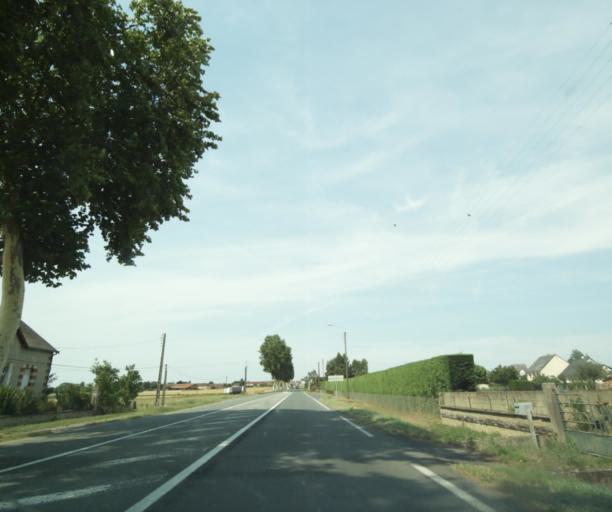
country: FR
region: Centre
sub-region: Departement d'Indre-et-Loire
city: La Celle-Saint-Avant
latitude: 47.0149
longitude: 0.6024
